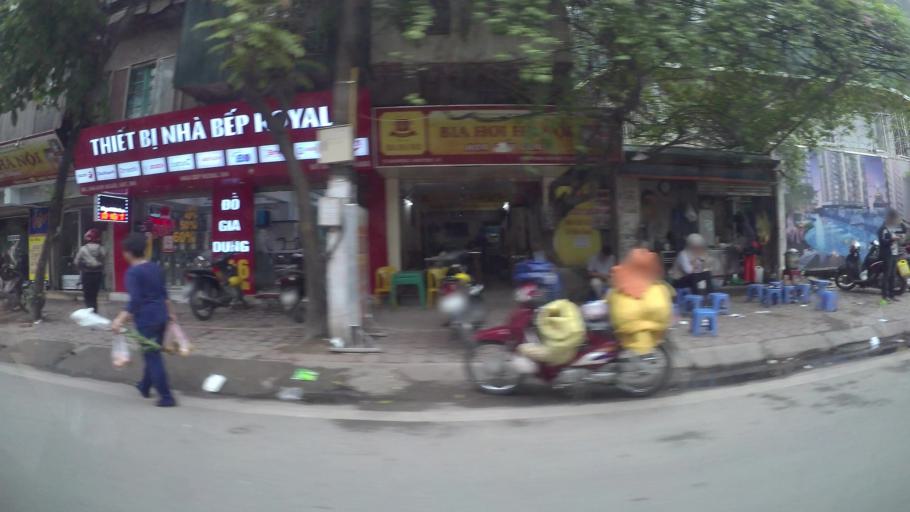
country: VN
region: Ha Noi
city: Hai BaTrung
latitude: 20.9975
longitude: 105.8618
